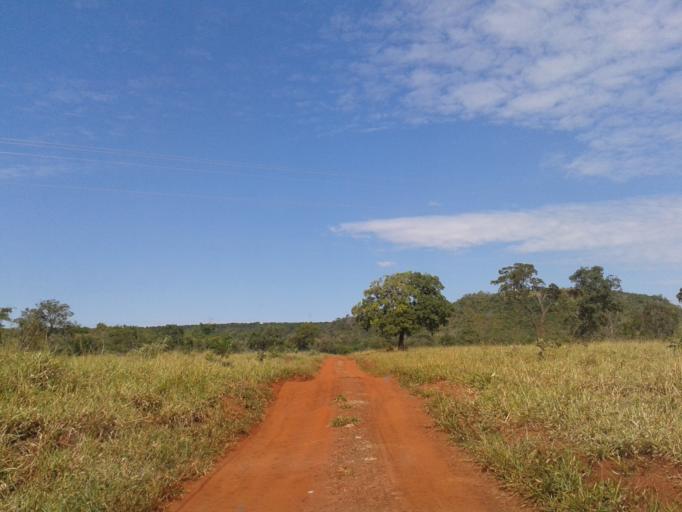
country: BR
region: Minas Gerais
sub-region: Campina Verde
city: Campina Verde
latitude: -19.3961
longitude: -49.7781
